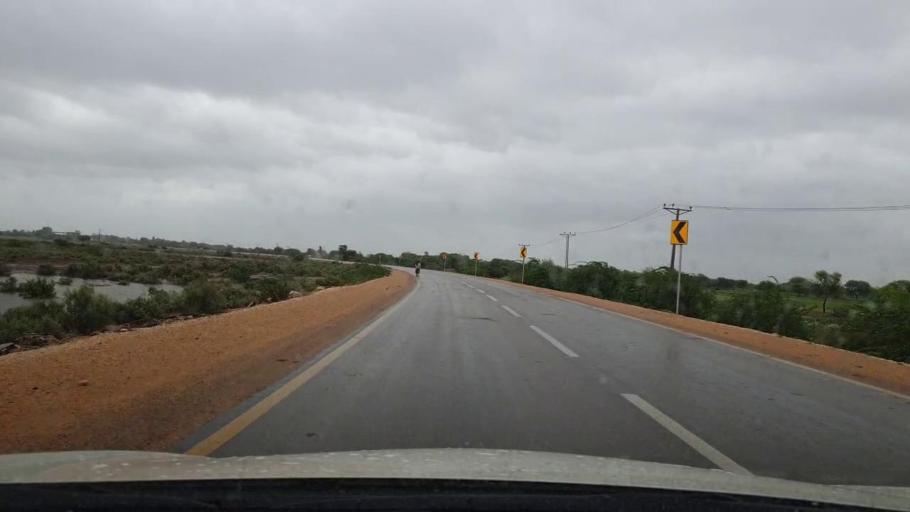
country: PK
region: Sindh
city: Kario
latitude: 24.6529
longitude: 68.6682
